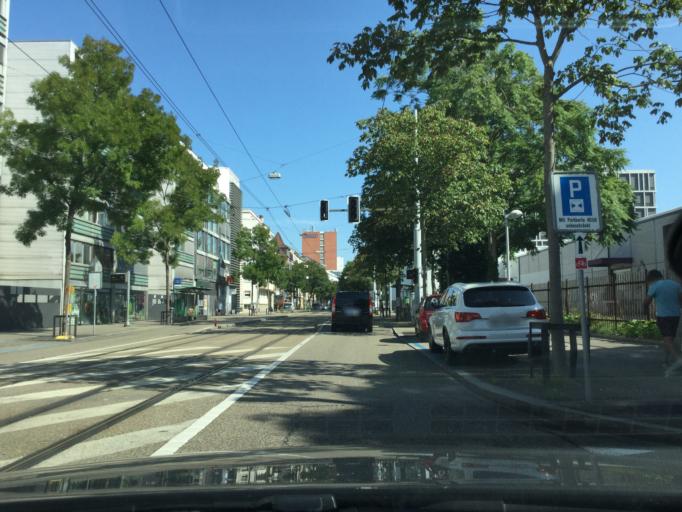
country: CH
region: Basel-City
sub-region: Basel-Stadt
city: Basel
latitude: 47.5684
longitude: 7.5974
